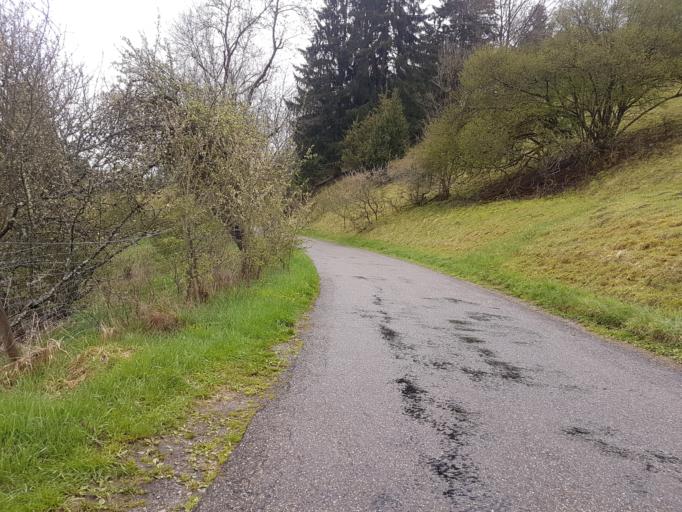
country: DE
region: Baden-Wuerttemberg
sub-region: Freiburg Region
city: Rottweil
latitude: 48.1920
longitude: 8.6123
